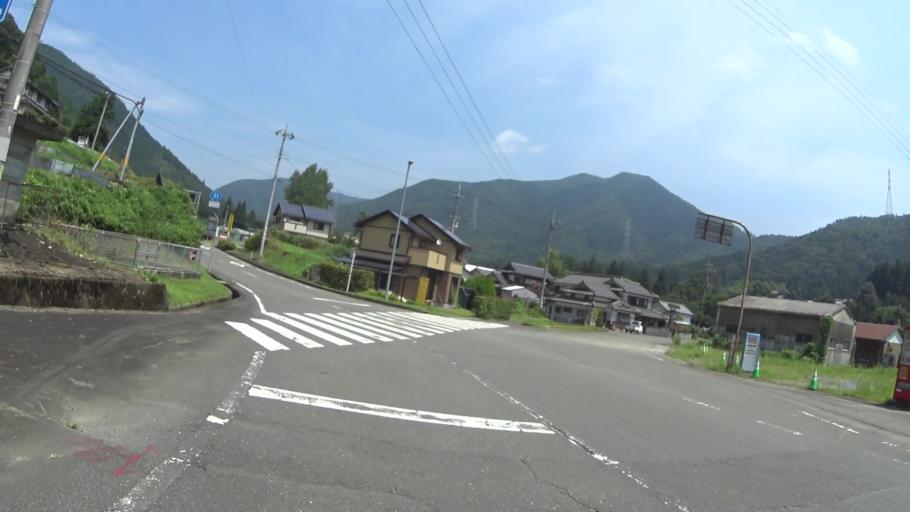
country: JP
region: Kyoto
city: Ayabe
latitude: 35.2648
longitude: 135.4308
